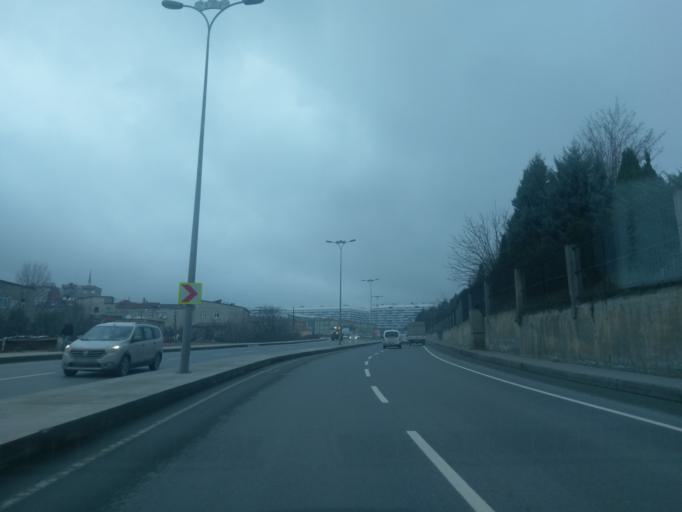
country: TR
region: Istanbul
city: Basaksehir
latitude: 41.0755
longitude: 28.7934
